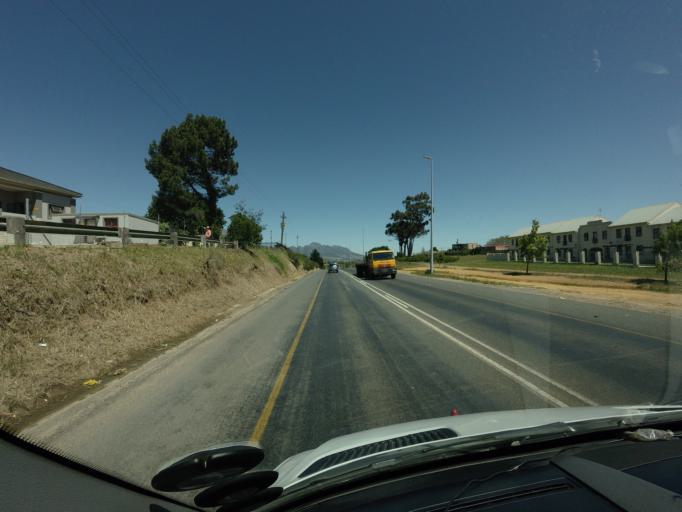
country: ZA
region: Western Cape
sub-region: Cape Winelands District Municipality
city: Stellenbosch
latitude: -33.9038
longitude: 18.8591
